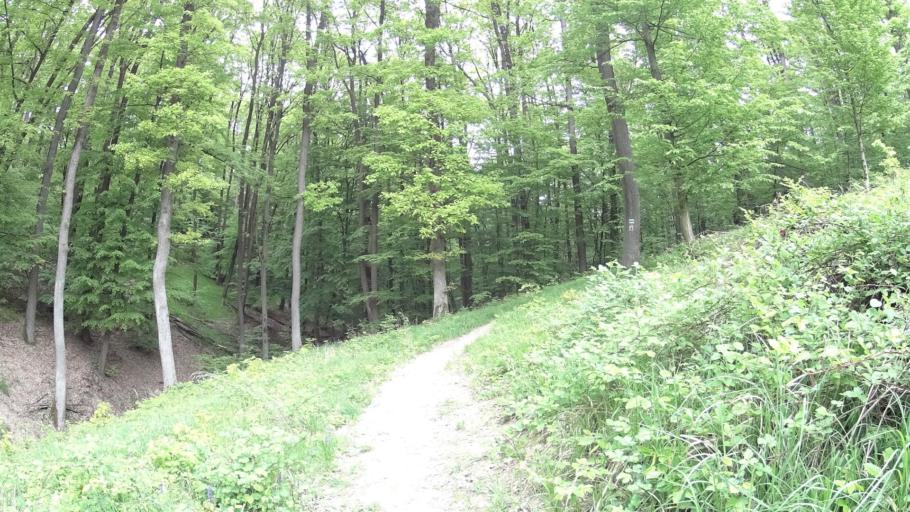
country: HU
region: Nograd
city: Romhany
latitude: 47.9010
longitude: 19.2417
